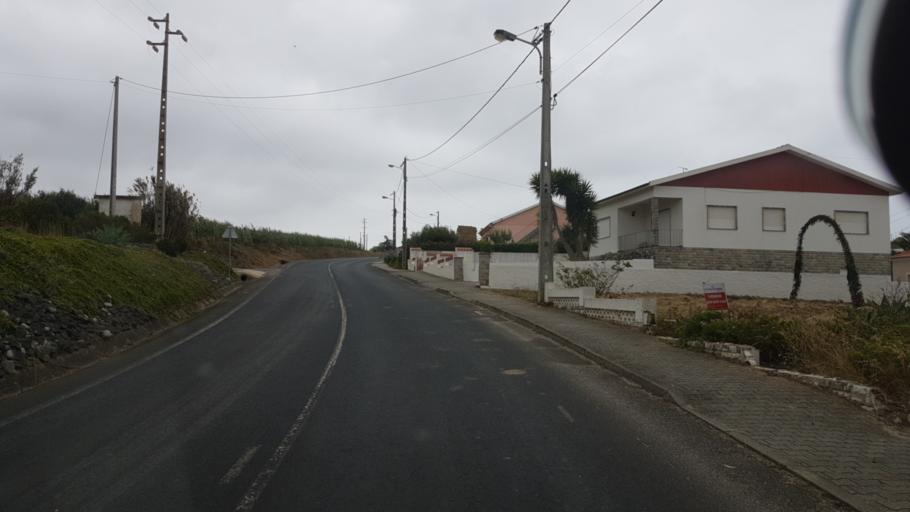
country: PT
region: Lisbon
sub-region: Lourinha
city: Lourinha
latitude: 39.2203
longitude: -9.3193
